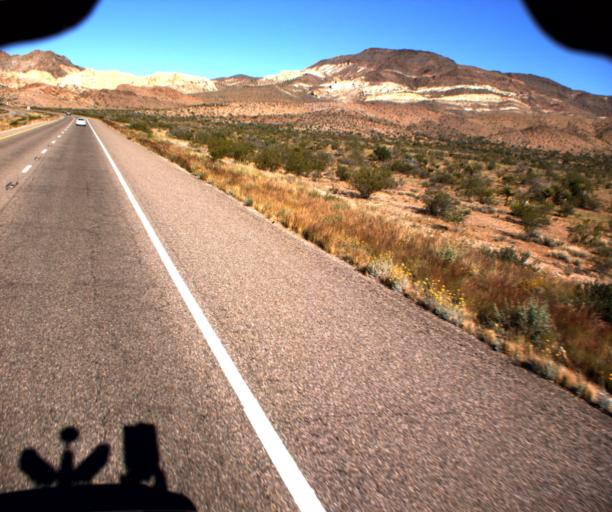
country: US
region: Arizona
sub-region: Mohave County
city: Golden Valley
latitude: 35.2292
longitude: -114.3646
